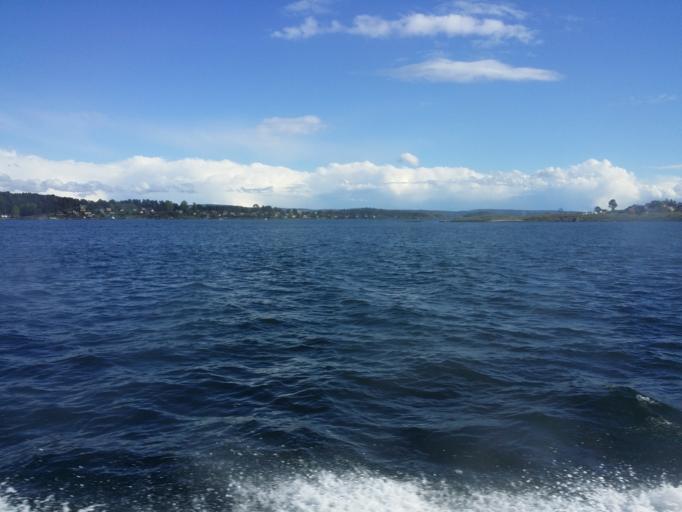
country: NO
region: Oslo
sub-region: Oslo
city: Sjolyststranda
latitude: 59.8954
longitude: 10.6952
